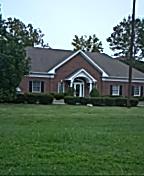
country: US
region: Kentucky
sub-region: Jefferson County
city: Middletown
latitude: 38.2466
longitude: -85.5303
